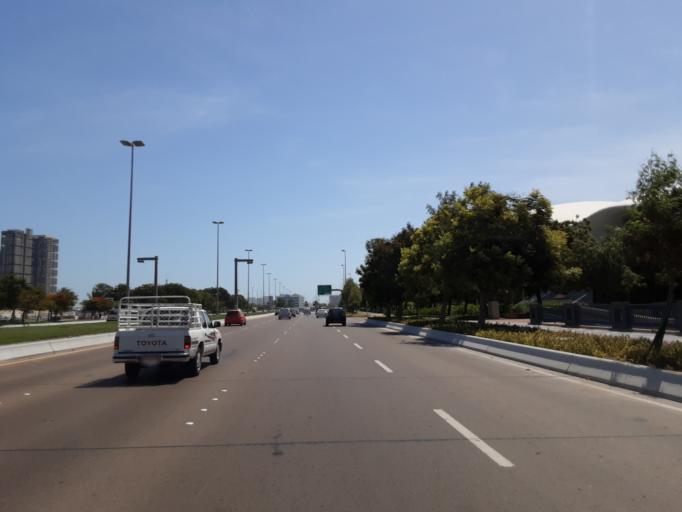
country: AE
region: Abu Dhabi
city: Abu Dhabi
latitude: 24.5086
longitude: 54.3734
